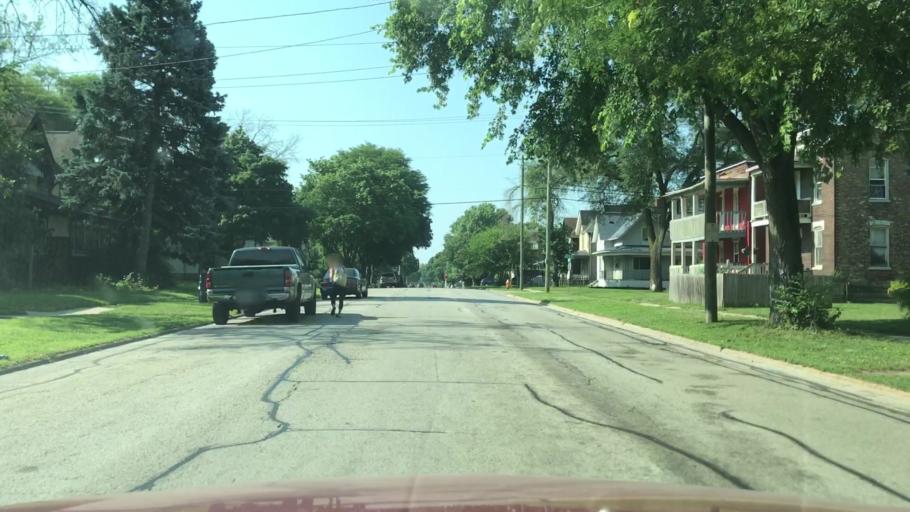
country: US
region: Illinois
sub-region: Winnebago County
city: Rockford
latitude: 42.2548
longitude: -89.0823
